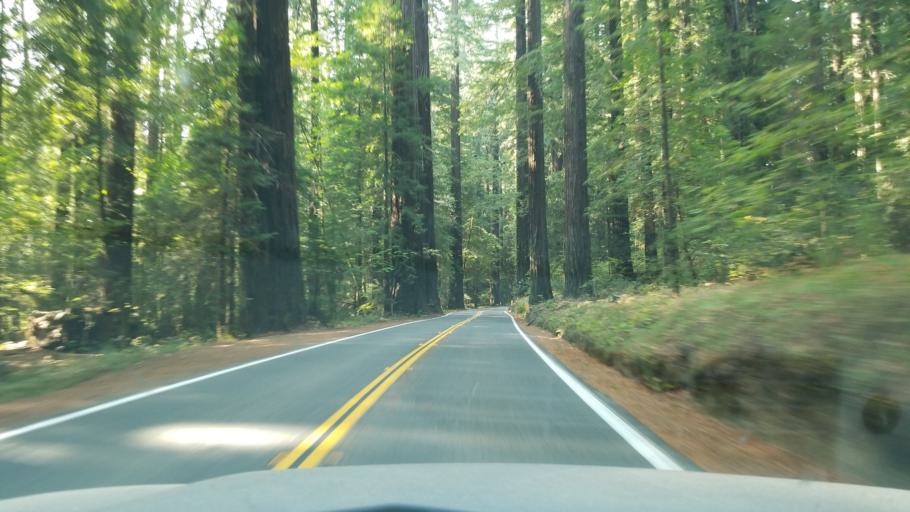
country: US
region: California
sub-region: Humboldt County
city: Redway
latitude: 40.2605
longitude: -123.8428
